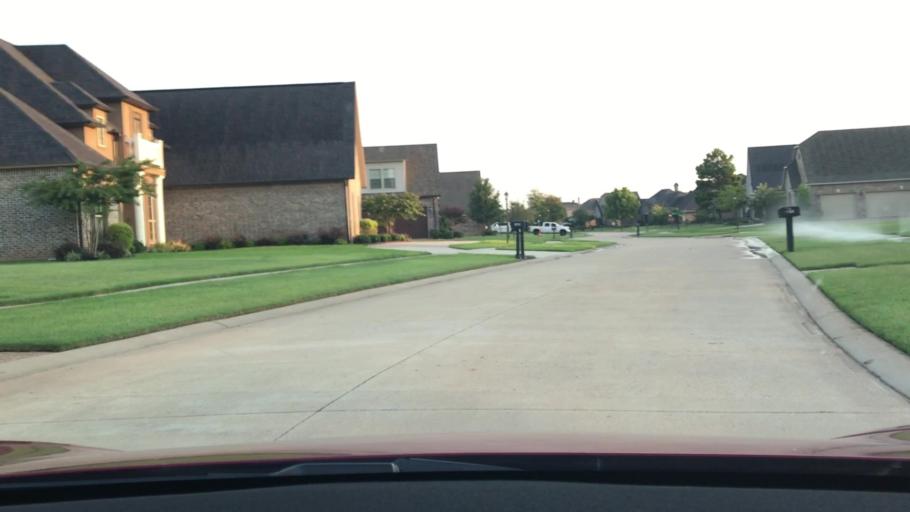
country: US
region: Louisiana
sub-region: Bossier Parish
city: Bossier City
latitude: 32.3906
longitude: -93.7014
